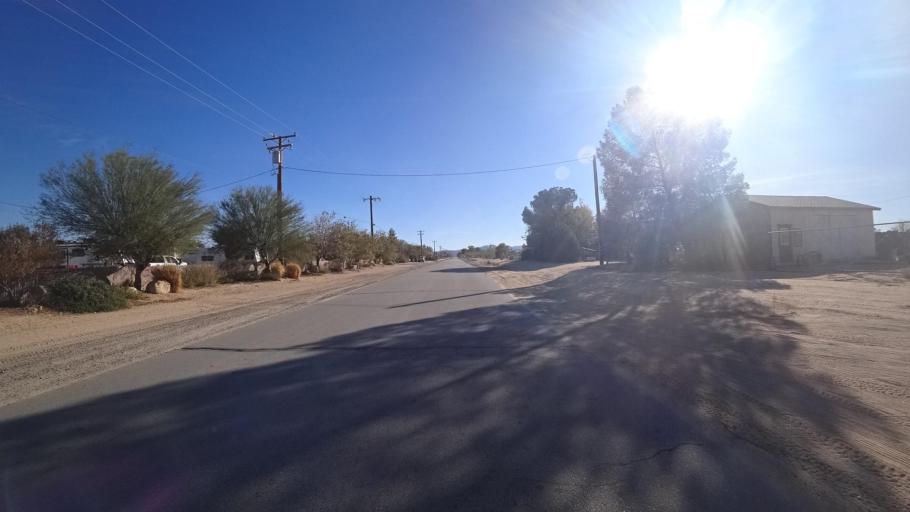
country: US
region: California
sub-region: Kern County
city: China Lake Acres
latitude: 35.6514
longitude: -117.7675
